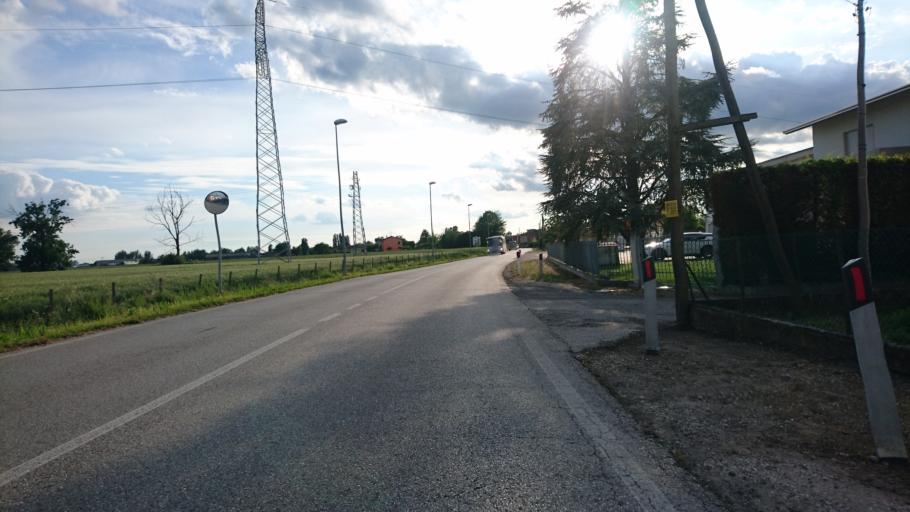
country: IT
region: Veneto
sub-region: Provincia di Rovigo
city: Trecenta
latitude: 45.0270
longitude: 11.4511
